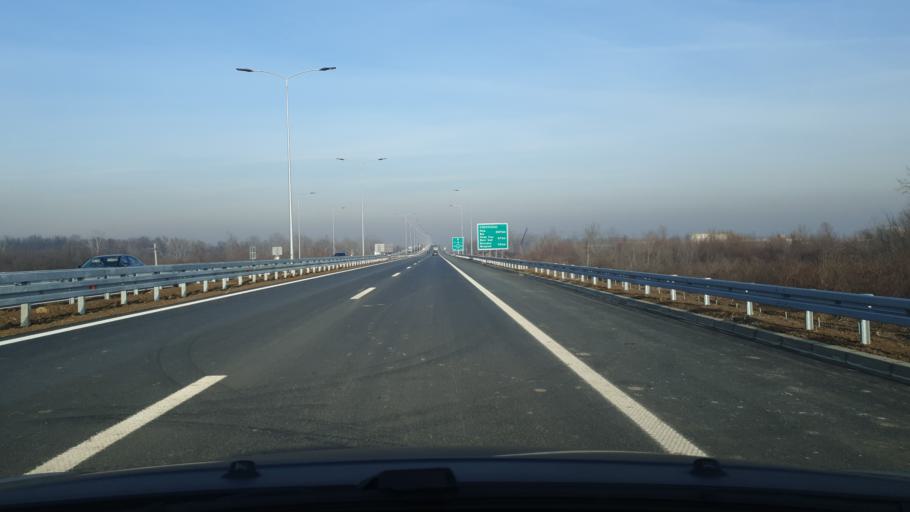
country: RS
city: Baric
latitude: 44.6558
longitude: 20.2358
